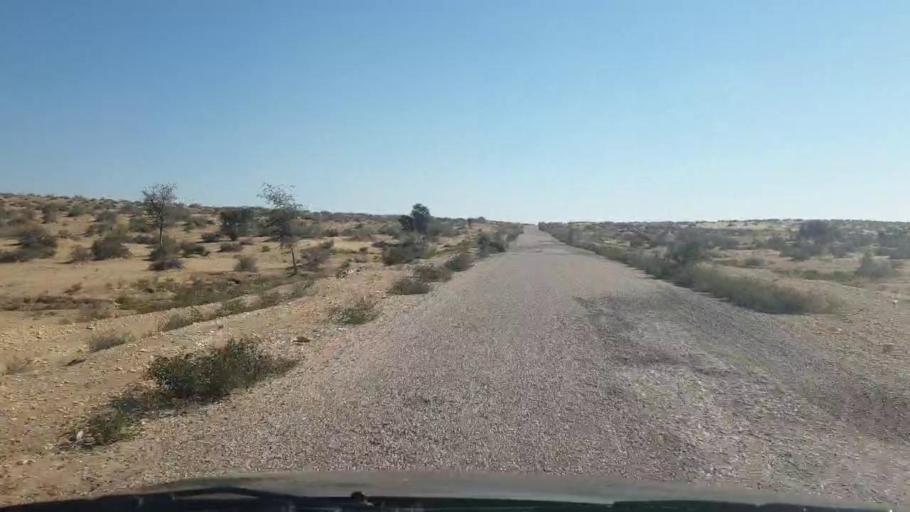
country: PK
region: Sindh
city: Bozdar
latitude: 27.0065
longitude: 68.8020
